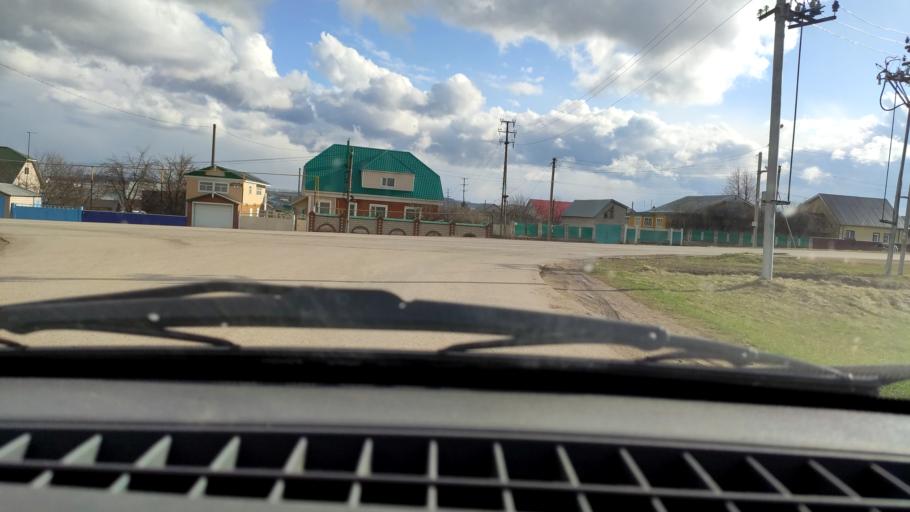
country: RU
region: Bashkortostan
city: Chekmagush
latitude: 55.1395
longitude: 54.6365
